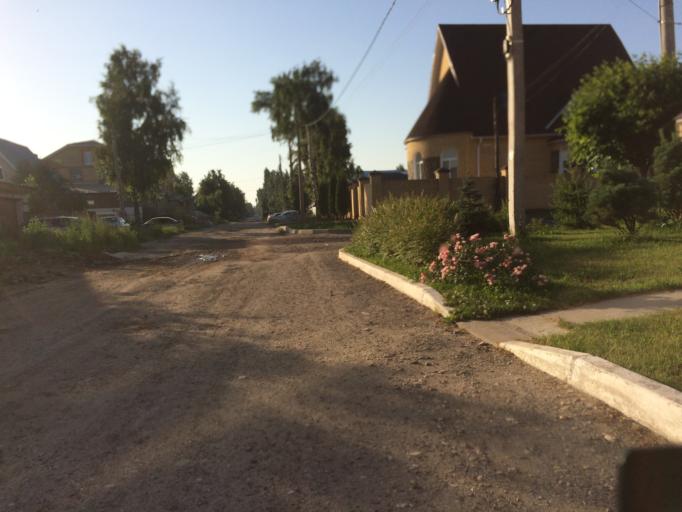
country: RU
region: Mariy-El
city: Yoshkar-Ola
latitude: 56.6531
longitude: 47.8932
